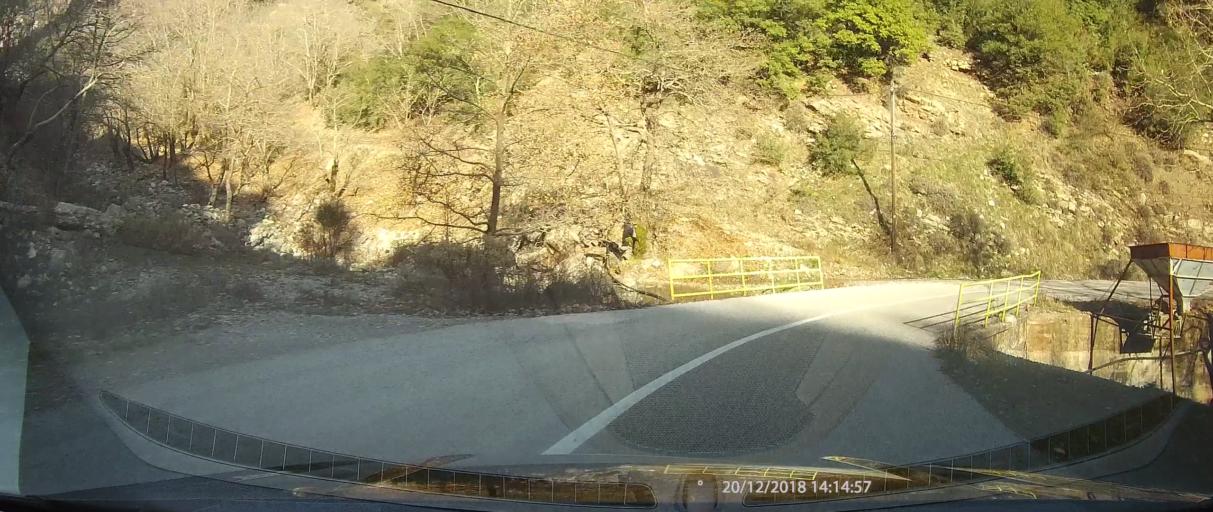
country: GR
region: West Greece
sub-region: Nomos Aitolias kai Akarnanias
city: Thermo
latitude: 38.7504
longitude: 21.6530
